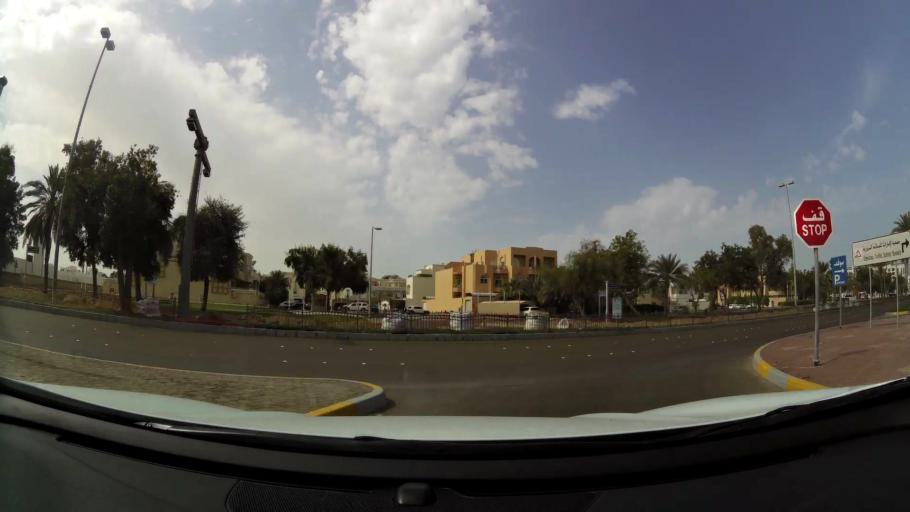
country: AE
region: Abu Dhabi
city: Abu Dhabi
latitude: 24.4543
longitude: 54.3578
